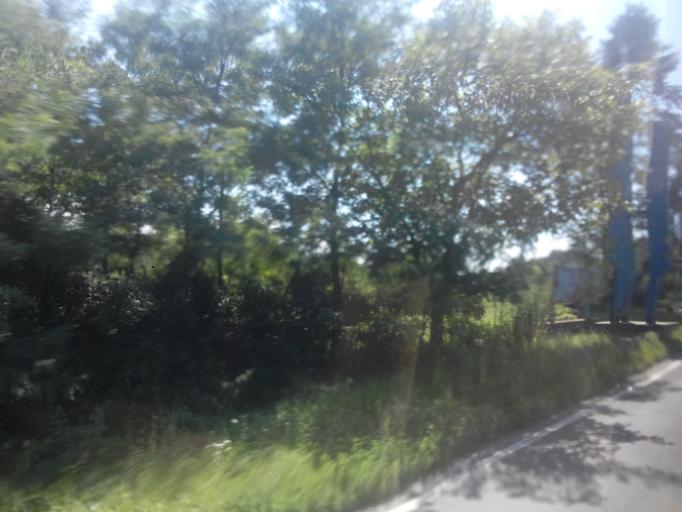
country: RO
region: Timis
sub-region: Comuna Pietroasa
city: Pietroasa
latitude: 45.8802
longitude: 22.3930
